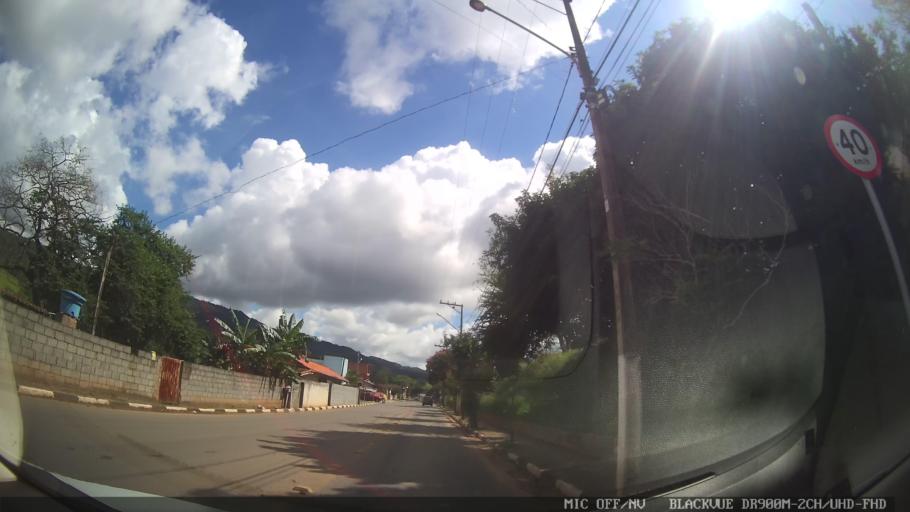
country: BR
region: Minas Gerais
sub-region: Extrema
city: Extrema
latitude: -22.8956
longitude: -46.4196
